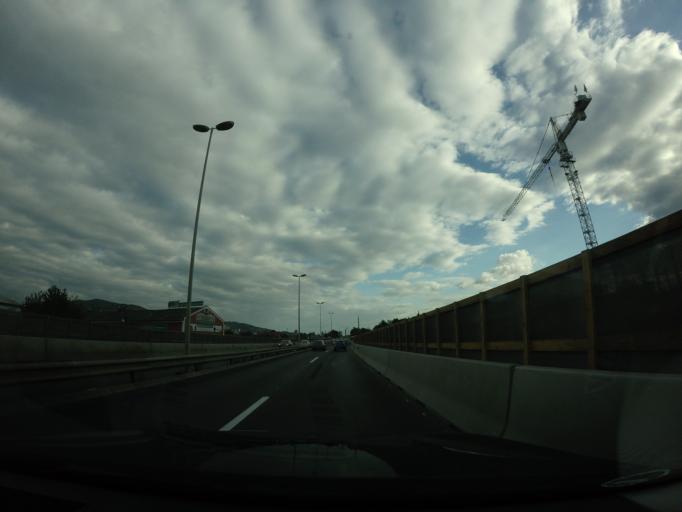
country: AT
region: Upper Austria
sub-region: Linz Stadt
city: Linz
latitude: 48.3156
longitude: 14.3053
